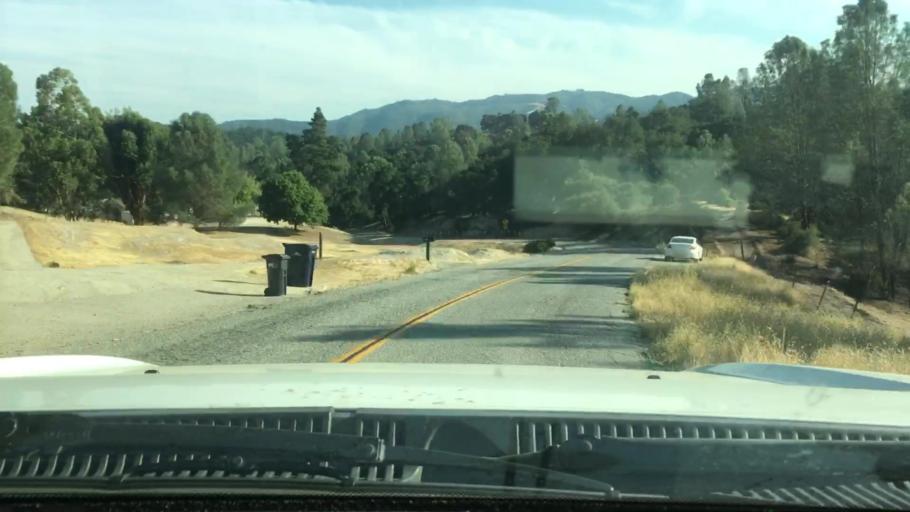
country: US
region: California
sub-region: San Luis Obispo County
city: Atascadero
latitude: 35.4545
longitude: -120.6540
